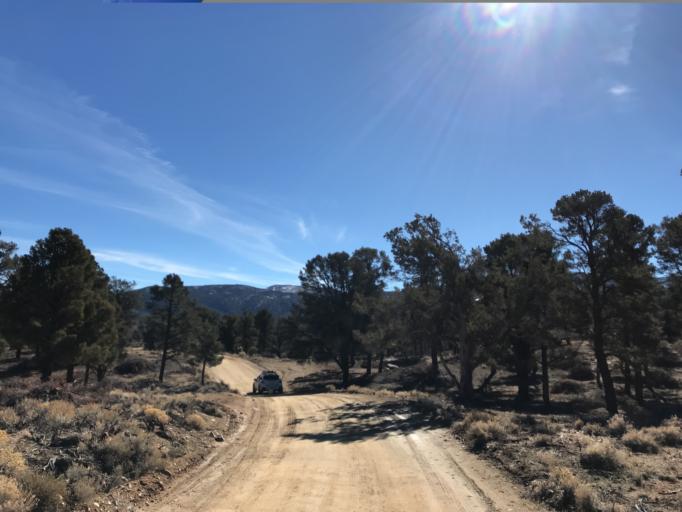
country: US
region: California
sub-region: San Bernardino County
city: Big Bear City
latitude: 34.2674
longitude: -116.7612
